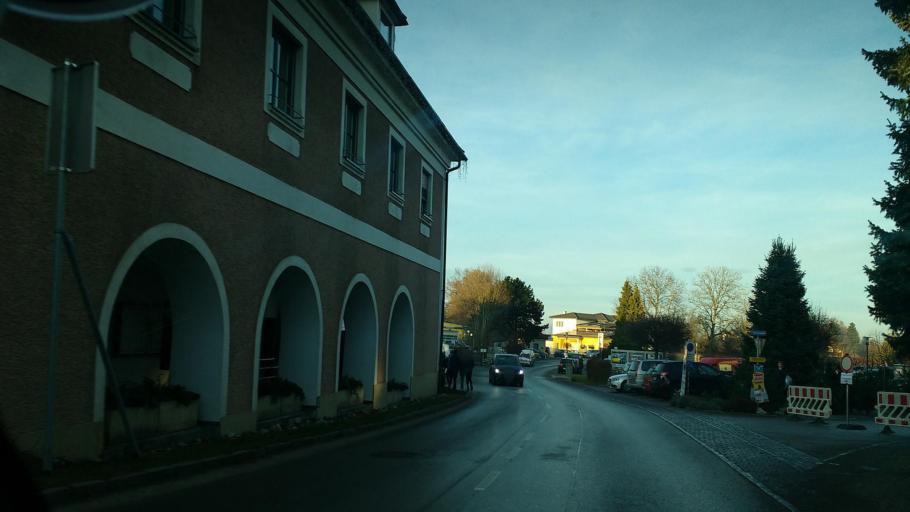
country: AT
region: Upper Austria
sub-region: Politischer Bezirk Gmunden
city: Scharnstein
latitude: 47.9612
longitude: 14.0165
